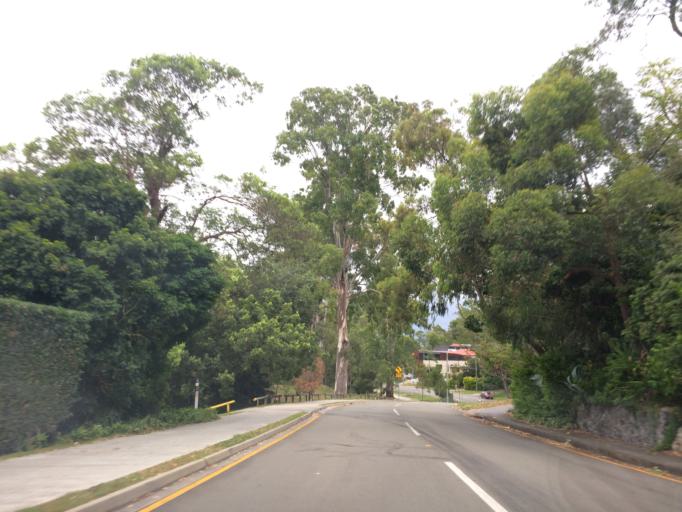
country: AU
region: Queensland
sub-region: Brisbane
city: Yeronga
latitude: -27.5024
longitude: 153.0076
